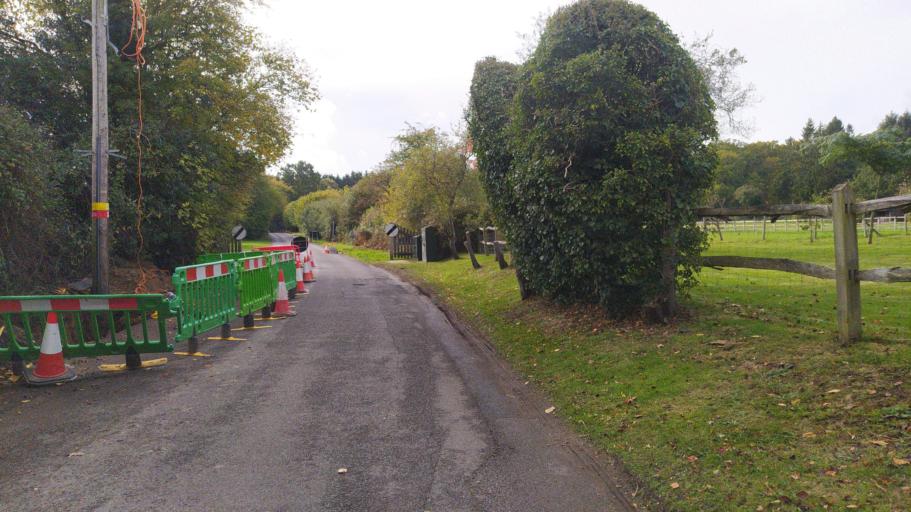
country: GB
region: England
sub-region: West Sussex
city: Midhurst
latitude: 50.9921
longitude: -0.7738
